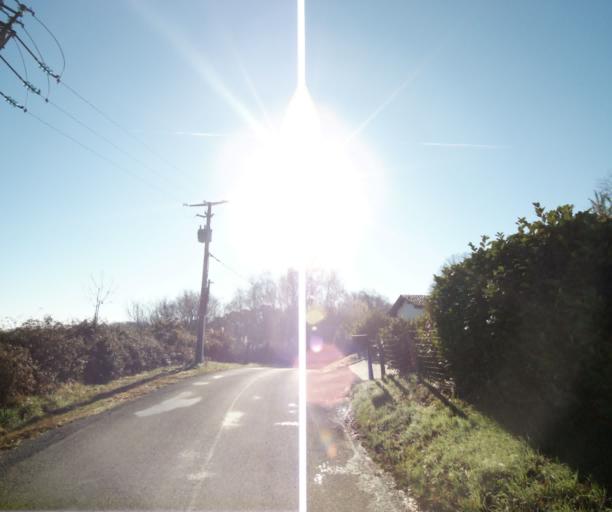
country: FR
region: Aquitaine
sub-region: Departement des Pyrenees-Atlantiques
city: Ciboure
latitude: 43.3665
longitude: -1.6625
